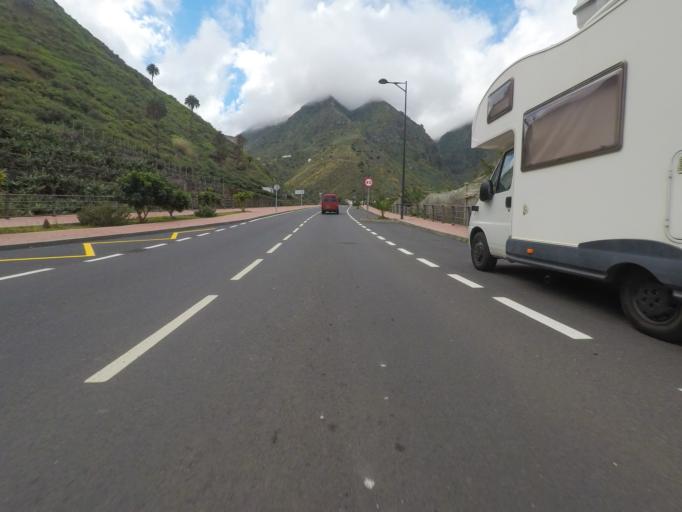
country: ES
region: Canary Islands
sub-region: Provincia de Santa Cruz de Tenerife
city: Hermigua
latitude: 28.1677
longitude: -17.1939
